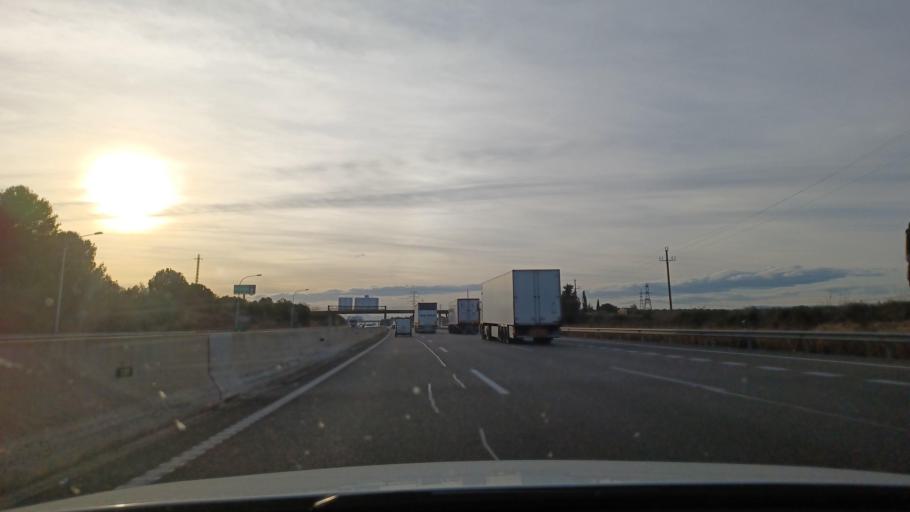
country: ES
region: Catalonia
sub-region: Provincia de Tarragona
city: Constanti
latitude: 41.1452
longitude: 1.2310
